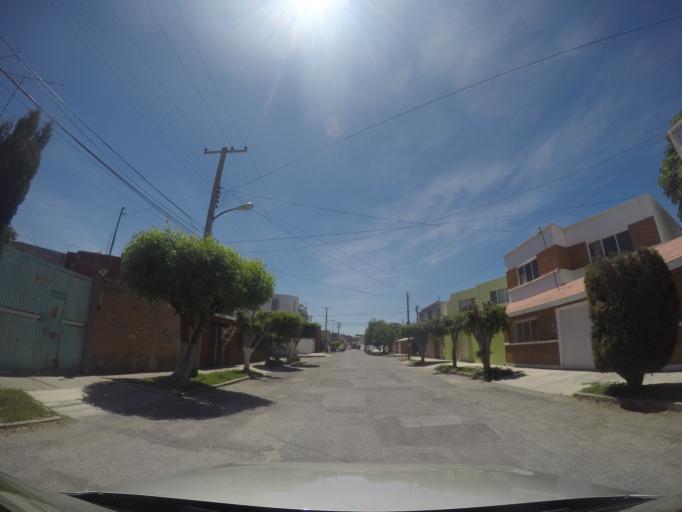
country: MX
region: San Luis Potosi
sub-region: San Luis Potosi
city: San Luis Potosi
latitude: 22.1578
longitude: -100.9877
